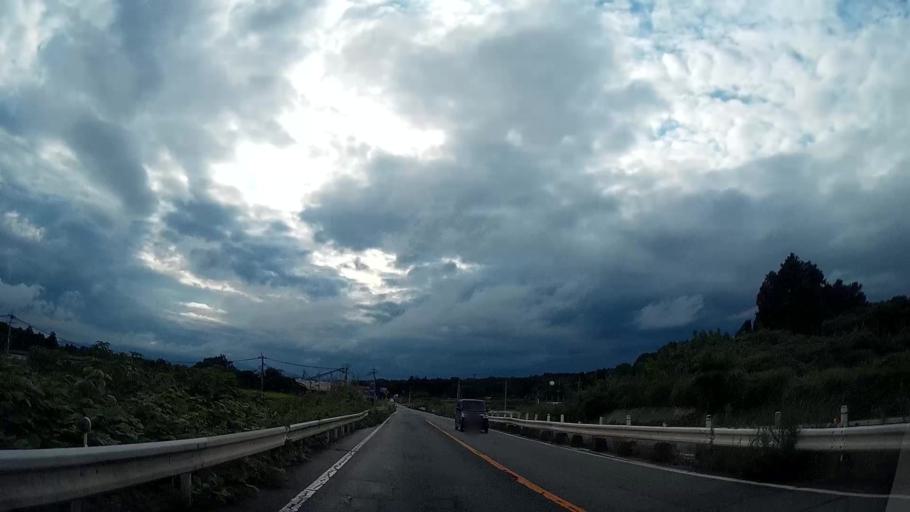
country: JP
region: Kumamoto
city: Ozu
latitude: 32.8783
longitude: 130.9151
